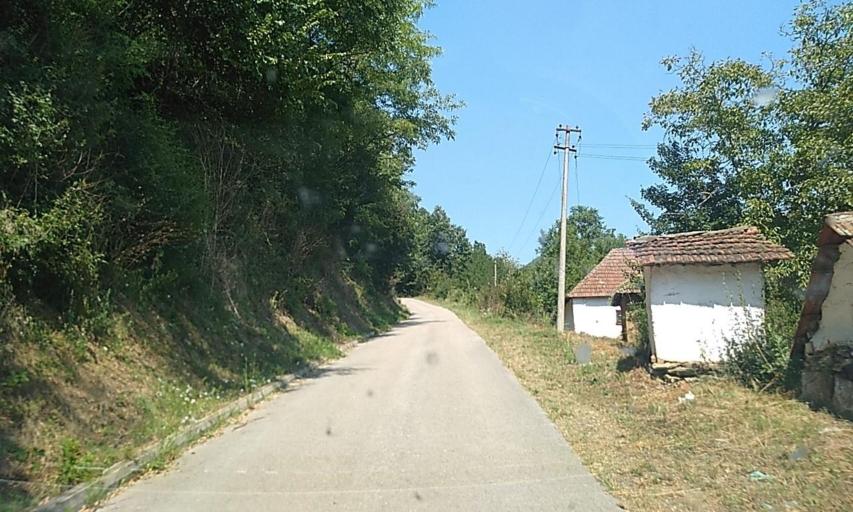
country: RS
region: Central Serbia
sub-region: Pcinjski Okrug
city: Vladicin Han
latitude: 42.7514
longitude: 22.0740
